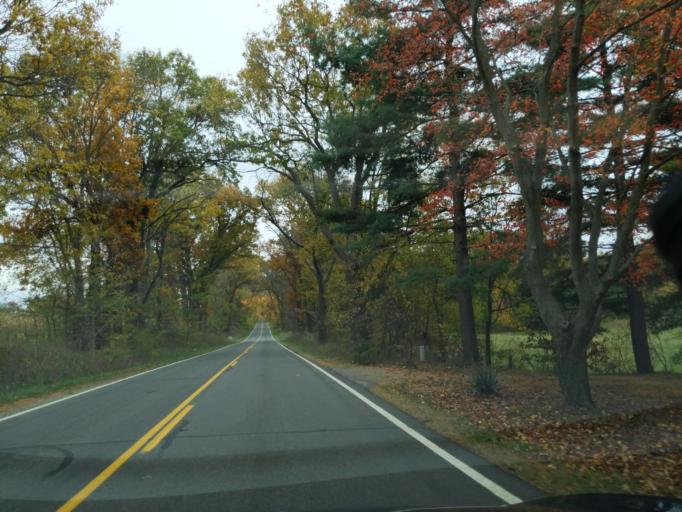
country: US
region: Michigan
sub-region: Eaton County
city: Eaton Rapids
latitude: 42.3836
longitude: -84.6005
